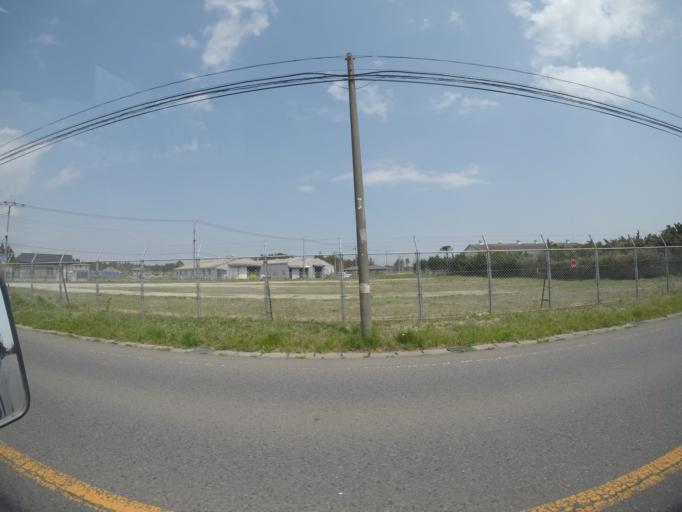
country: JP
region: Chiba
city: Sawara
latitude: 35.8589
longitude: 140.5543
